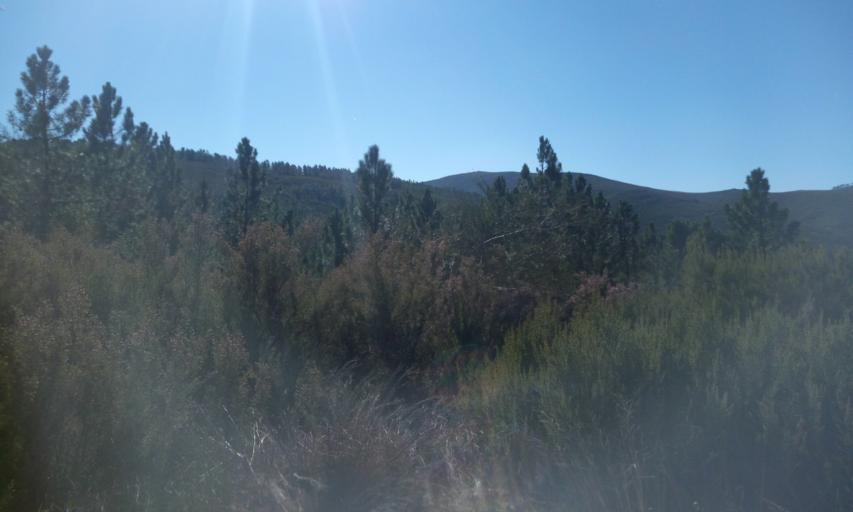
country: PT
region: Guarda
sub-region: Manteigas
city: Manteigas
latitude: 40.4447
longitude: -7.5078
